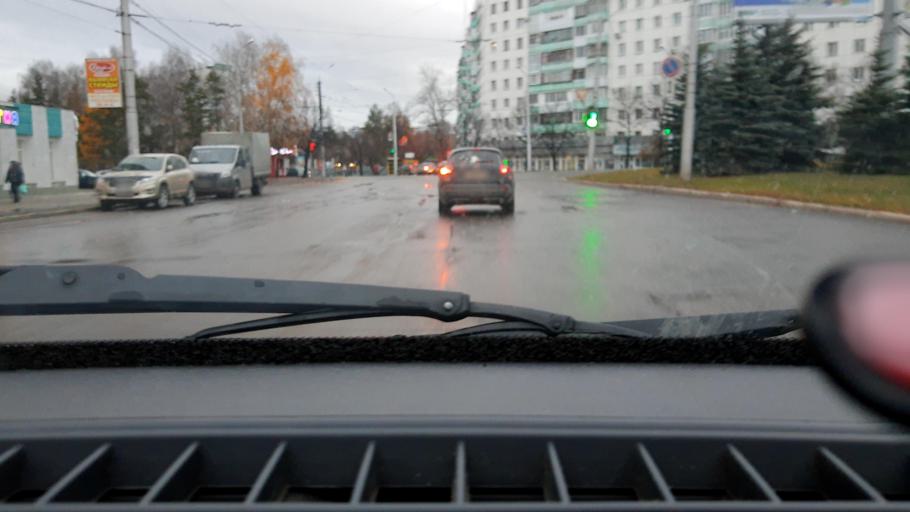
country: RU
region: Bashkortostan
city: Ufa
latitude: 54.7442
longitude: 56.0265
